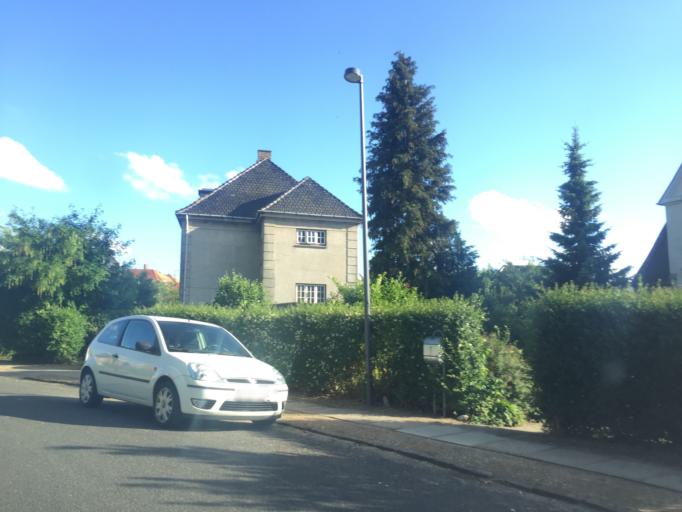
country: DK
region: Capital Region
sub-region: Kobenhavn
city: Vanlose
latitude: 55.7065
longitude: 12.4959
